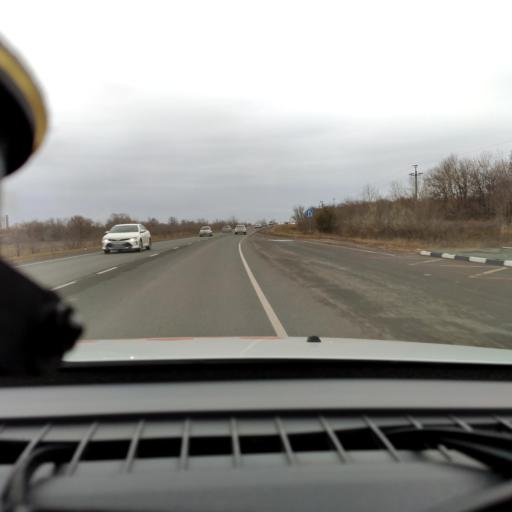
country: RU
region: Samara
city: Samara
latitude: 53.1234
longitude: 50.1930
